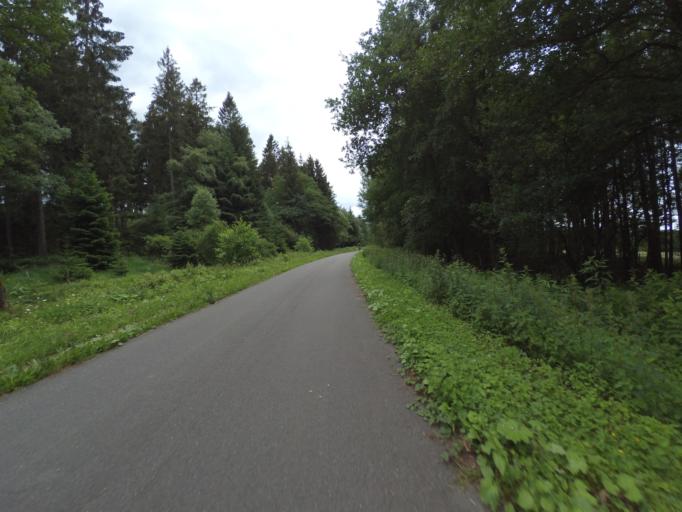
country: DE
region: North Rhine-Westphalia
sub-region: Regierungsbezirk Koln
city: Roetgen
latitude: 50.6431
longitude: 6.2256
